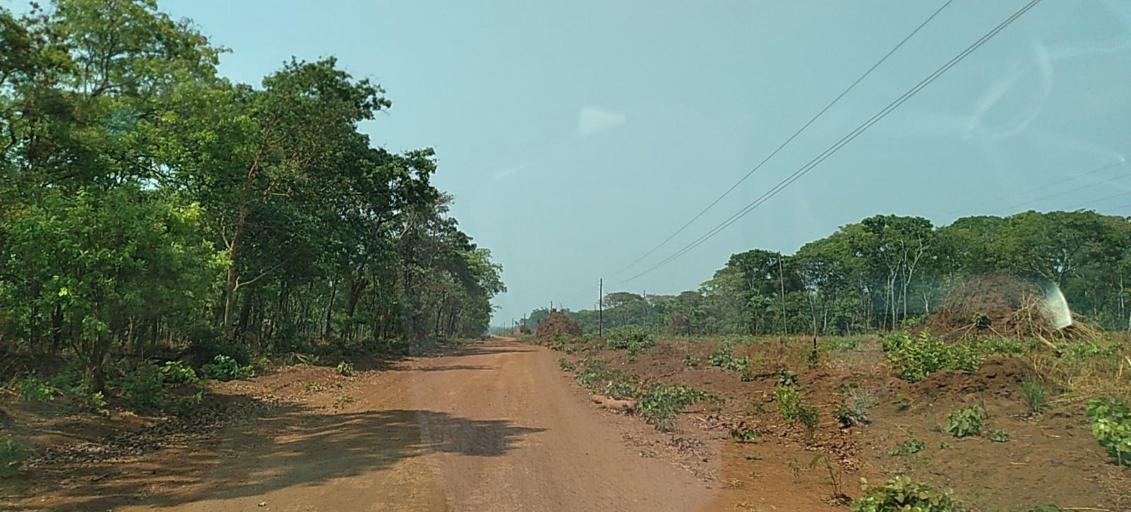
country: ZM
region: Copperbelt
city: Kalulushi
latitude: -13.0759
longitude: 27.4128
